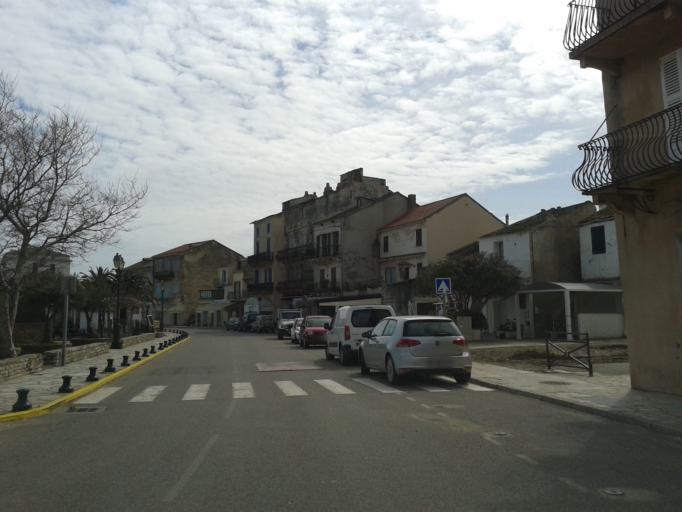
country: FR
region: Corsica
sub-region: Departement de la Haute-Corse
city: Brando
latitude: 42.9588
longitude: 9.4533
